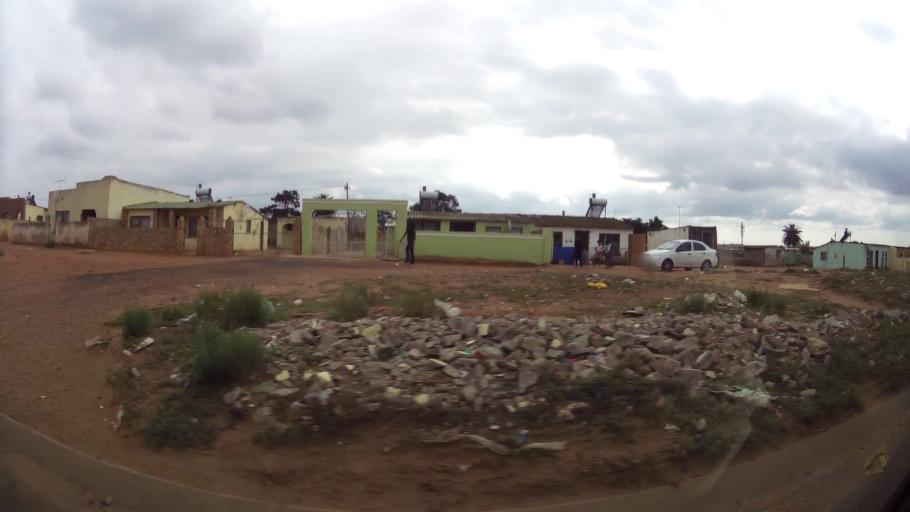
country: ZA
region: Eastern Cape
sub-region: Nelson Mandela Bay Metropolitan Municipality
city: Port Elizabeth
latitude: -33.8674
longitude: 25.5694
